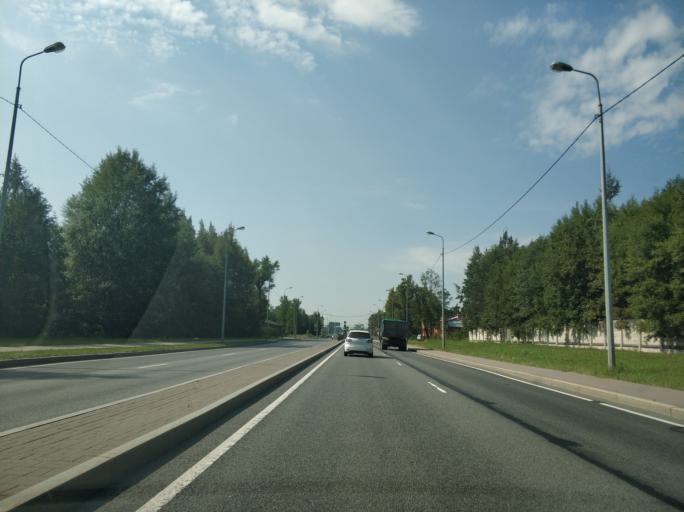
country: RU
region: St.-Petersburg
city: Krasnogvargeisky
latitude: 59.9890
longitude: 30.5264
